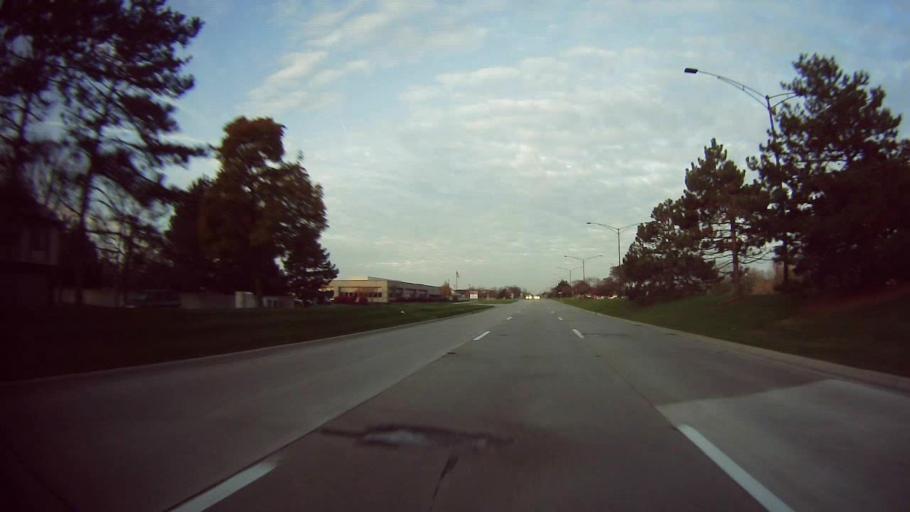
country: US
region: Michigan
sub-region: Oakland County
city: Clawson
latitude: 42.5636
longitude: -83.1031
